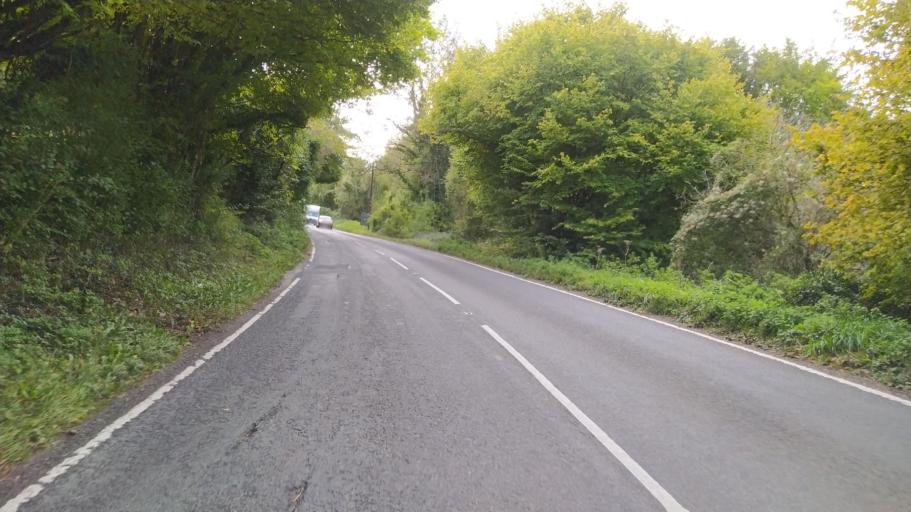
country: GB
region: England
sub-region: Hampshire
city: Romsey
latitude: 51.0481
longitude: -1.5179
